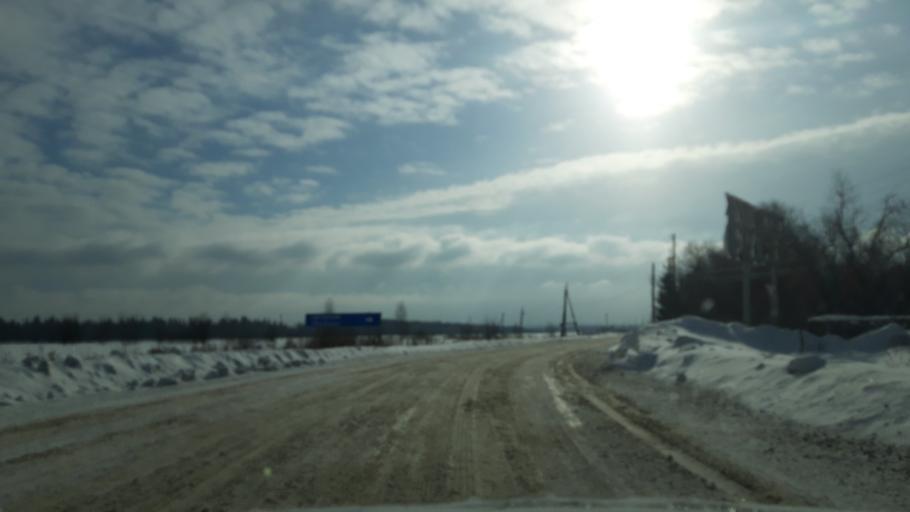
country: RU
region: Moskovskaya
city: Yermolino
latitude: 56.1400
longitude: 37.3799
